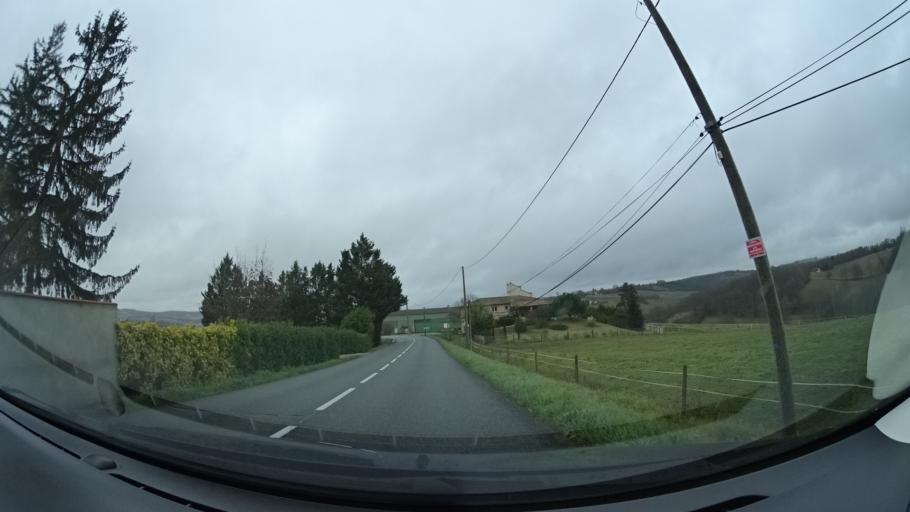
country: FR
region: Midi-Pyrenees
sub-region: Departement du Tarn-et-Garonne
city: Lauzerte
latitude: 44.2076
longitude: 1.1372
